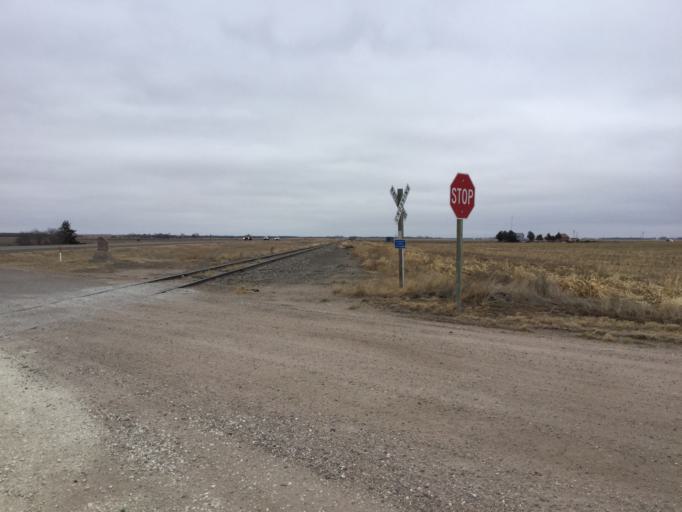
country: US
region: Kansas
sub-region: Pawnee County
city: Larned
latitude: 38.2233
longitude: -99.0407
